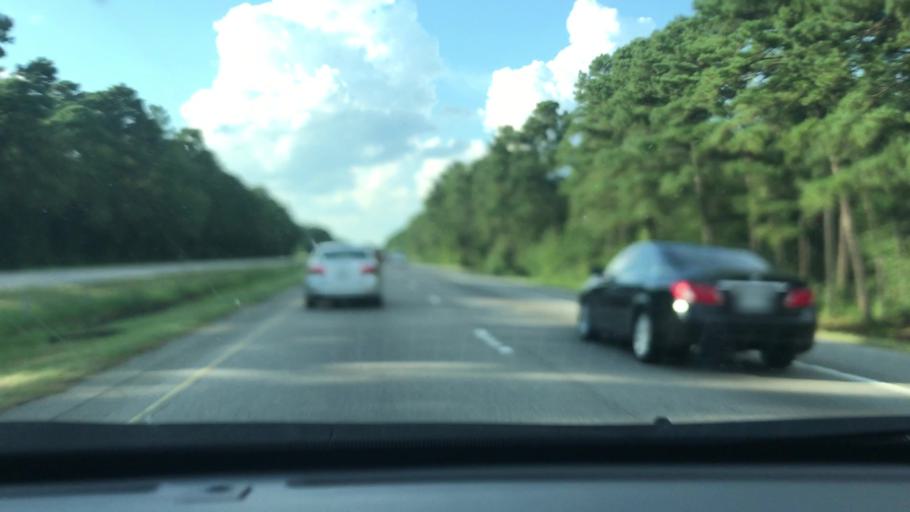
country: US
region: North Carolina
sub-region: Robeson County
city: Saint Pauls
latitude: 34.7504
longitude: -78.9970
